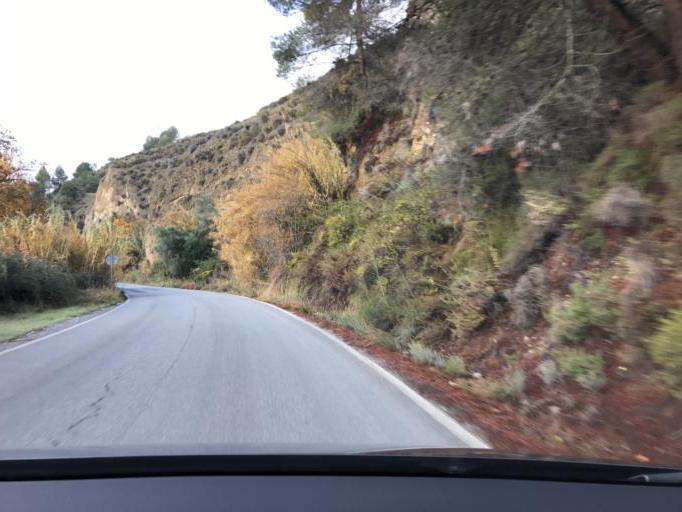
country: ES
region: Andalusia
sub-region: Provincia de Granada
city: Dudar
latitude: 37.1890
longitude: -3.4773
